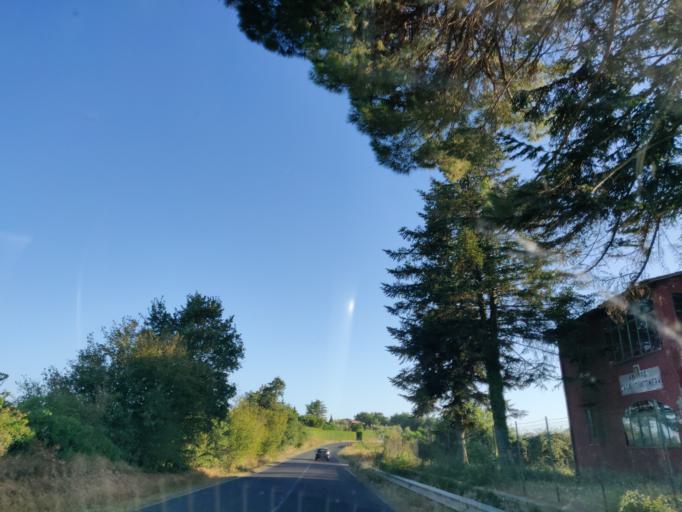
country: IT
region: Latium
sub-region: Provincia di Viterbo
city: Gradoli
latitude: 42.6622
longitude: 11.8525
